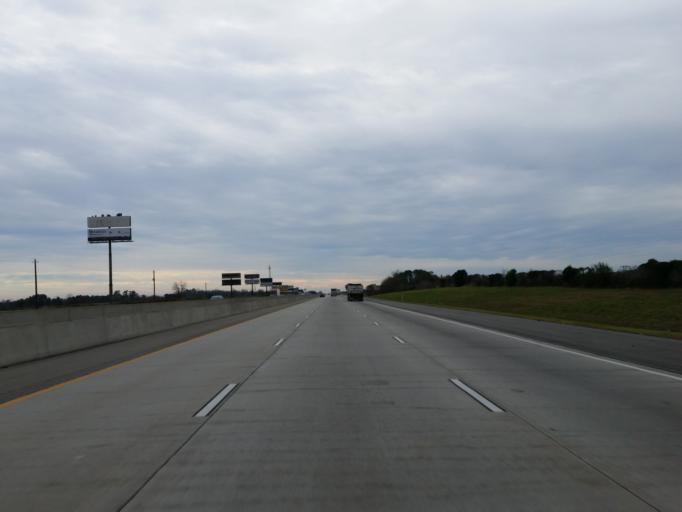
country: US
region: Georgia
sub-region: Tift County
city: Unionville
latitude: 31.3855
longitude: -83.4971
